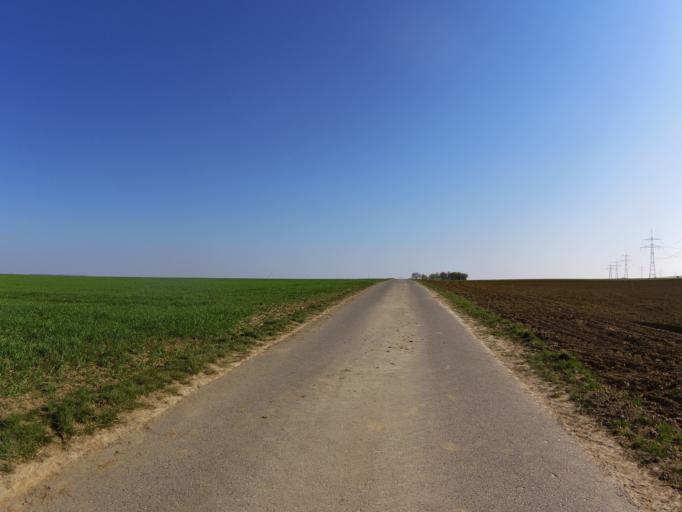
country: DE
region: Bavaria
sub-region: Regierungsbezirk Unterfranken
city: Oberpleichfeld
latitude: 49.8308
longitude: 10.0904
